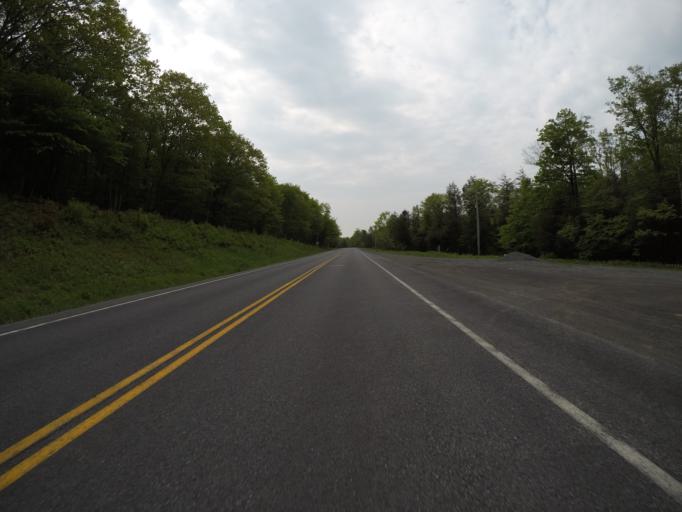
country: US
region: New York
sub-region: Sullivan County
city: Livingston Manor
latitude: 42.0351
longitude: -74.8994
